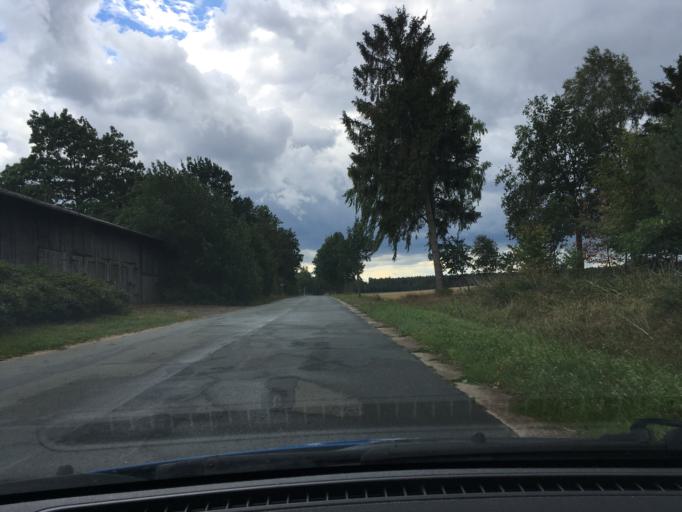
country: DE
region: Lower Saxony
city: Wietzendorf
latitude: 52.9109
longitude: 10.0142
